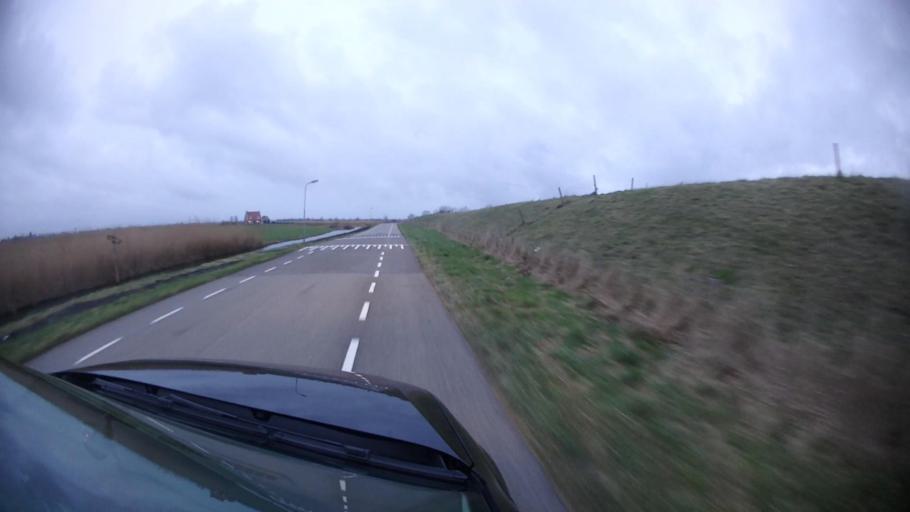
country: NL
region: North Holland
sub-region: Gemeente Edam-Volendam
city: Volendam
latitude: 52.4749
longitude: 5.0631
